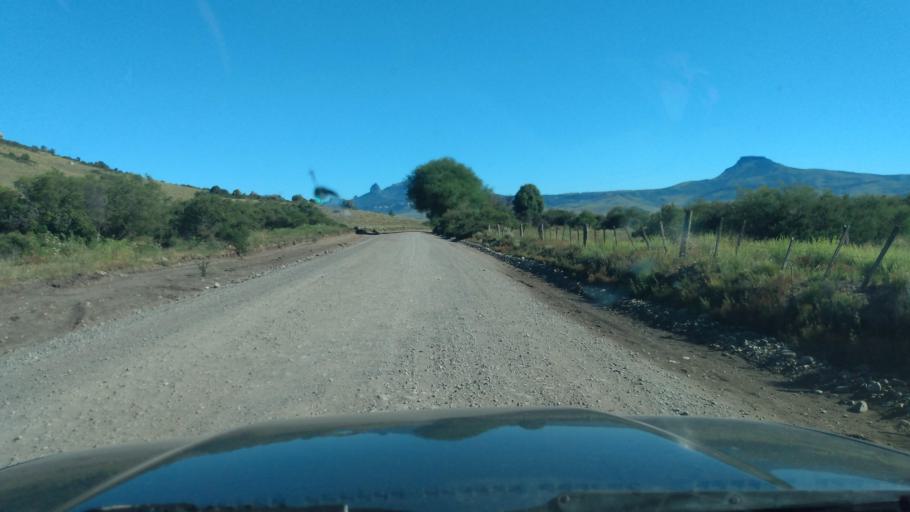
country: AR
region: Neuquen
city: Junin de los Andes
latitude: -39.8399
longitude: -71.1888
